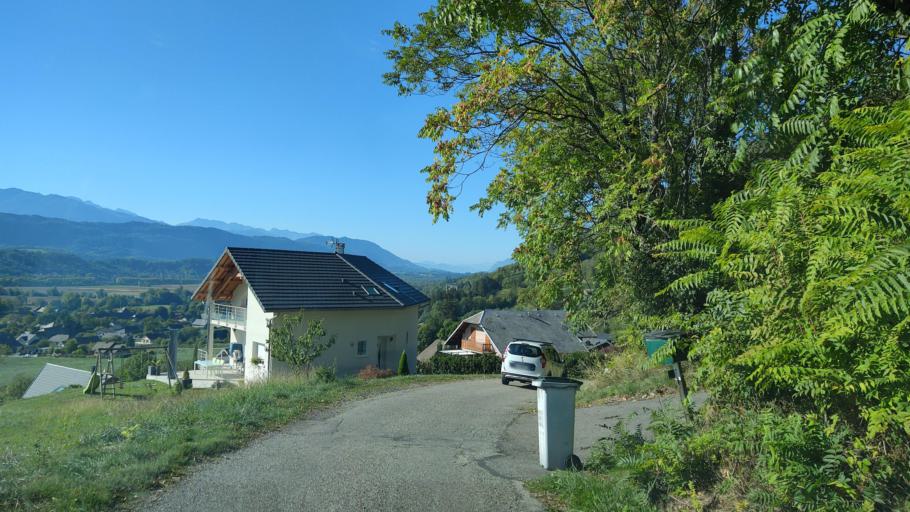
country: FR
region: Rhone-Alpes
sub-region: Departement de la Savoie
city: Coise-Saint-Jean-Pied-Gauthier
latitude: 45.5626
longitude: 6.1308
